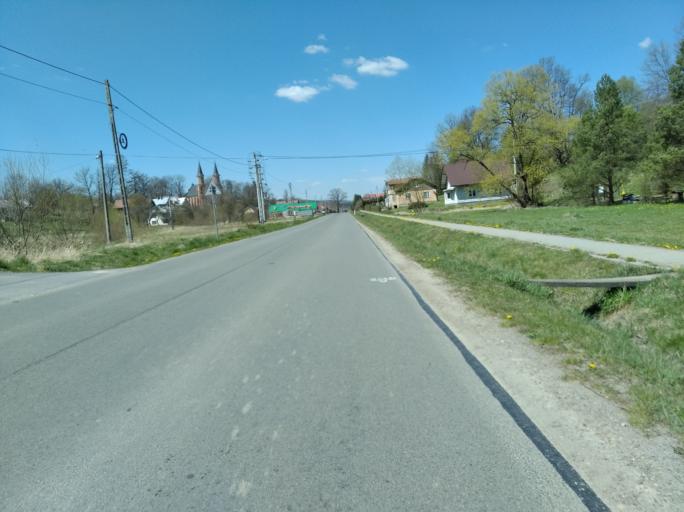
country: PL
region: Subcarpathian Voivodeship
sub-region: Powiat brzozowski
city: Dydnia
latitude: 49.6827
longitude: 22.1810
